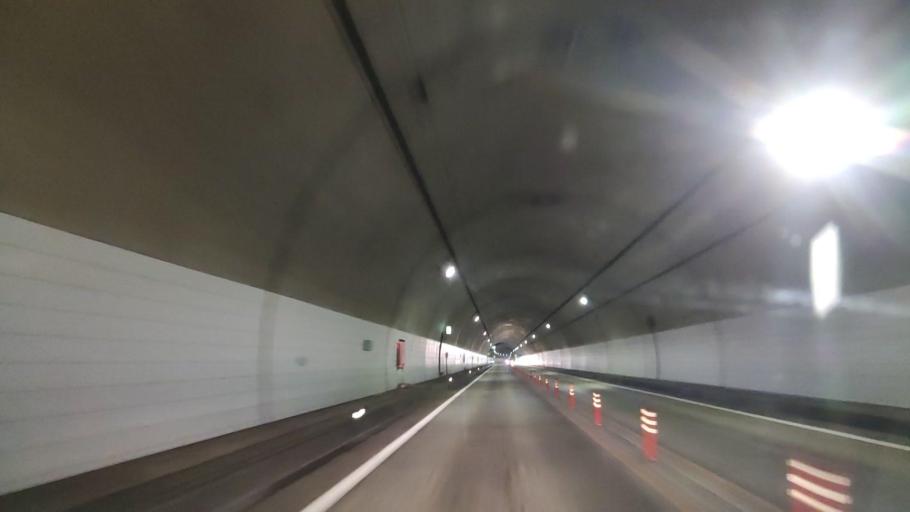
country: JP
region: Akita
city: Odate
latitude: 40.3647
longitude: 140.6972
